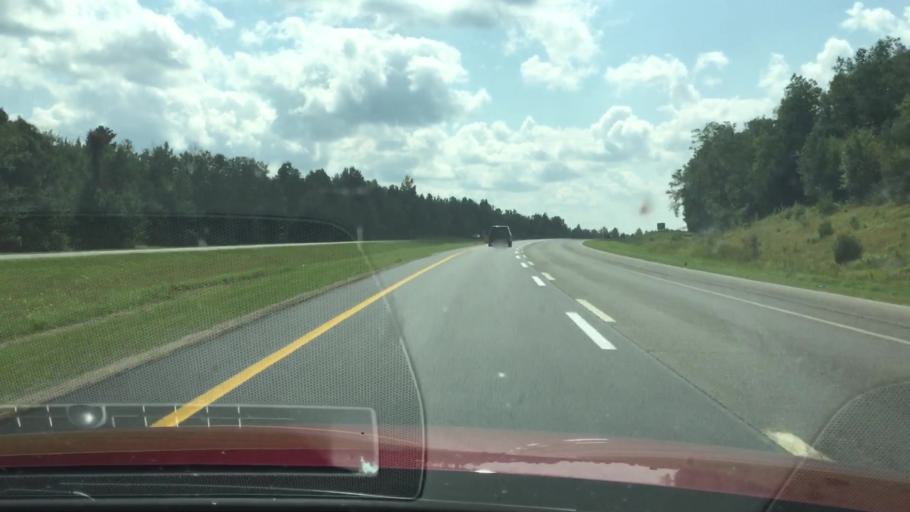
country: US
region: Maine
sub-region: Penobscot County
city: Medway
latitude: 45.6190
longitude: -68.5095
